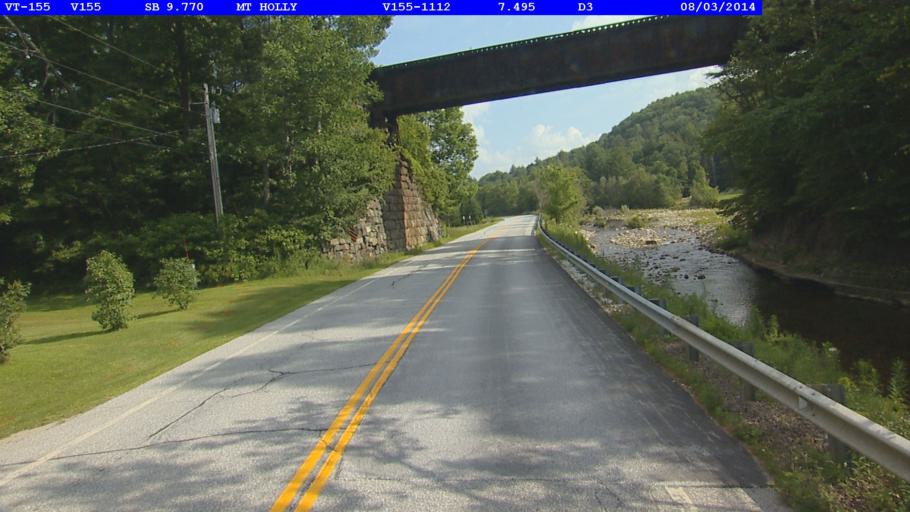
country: US
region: Vermont
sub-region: Rutland County
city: Rutland
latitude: 43.4466
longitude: -72.8715
